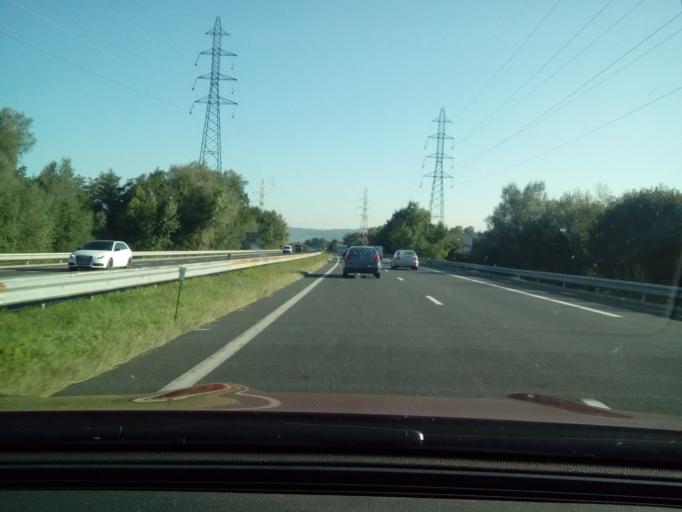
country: FR
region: Rhone-Alpes
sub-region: Departement de la Haute-Savoie
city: Seynod
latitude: 45.8851
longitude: 6.0812
